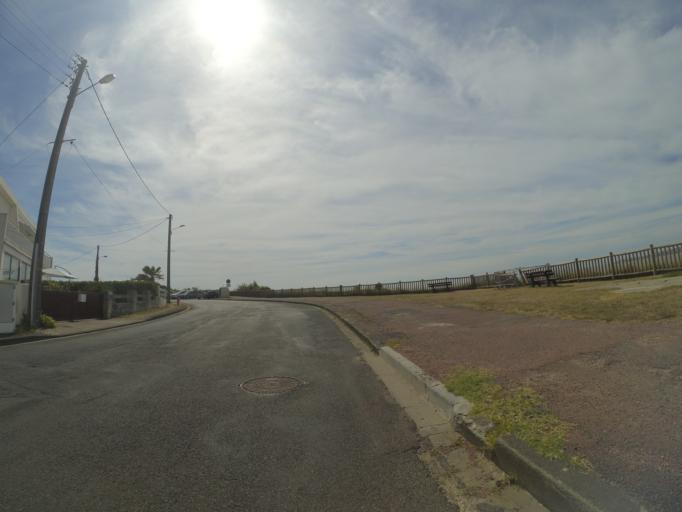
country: FR
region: Poitou-Charentes
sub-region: Departement de la Charente-Maritime
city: Saint-Georges-de-Didonne
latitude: 45.6047
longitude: -1.0119
